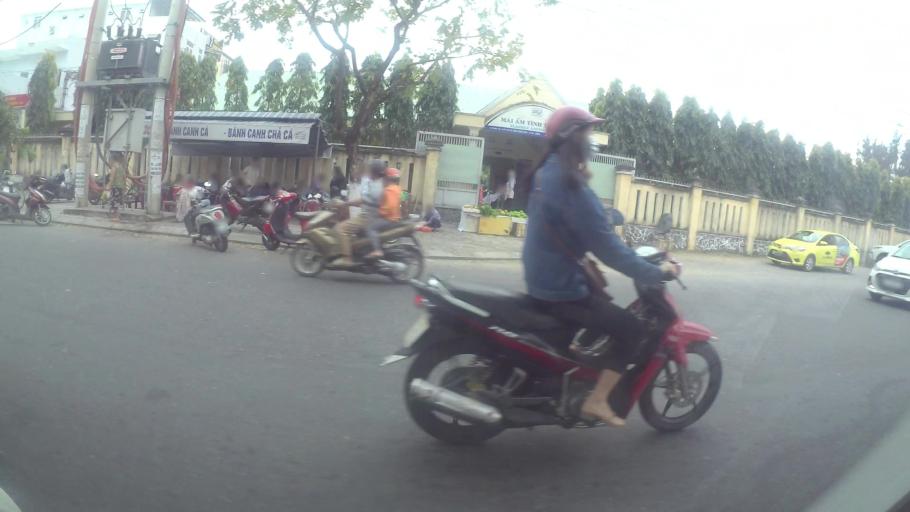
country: VN
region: Da Nang
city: Son Tra
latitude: 16.0461
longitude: 108.2443
